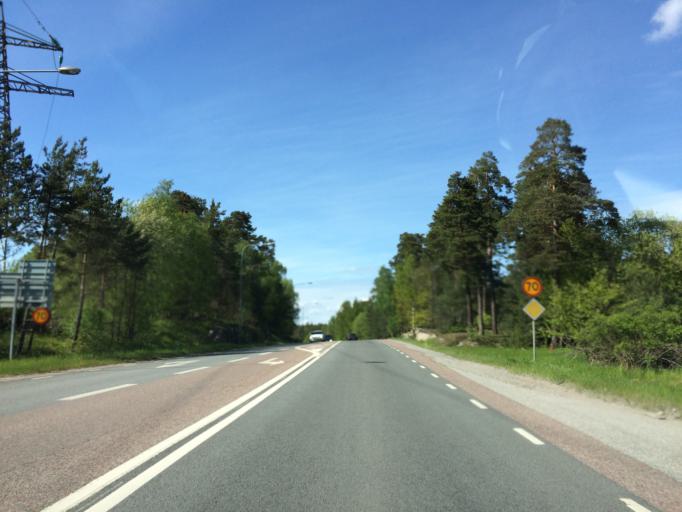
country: SE
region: Stockholm
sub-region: Sollentuna Kommun
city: Sollentuna
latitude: 59.4343
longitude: 17.9923
